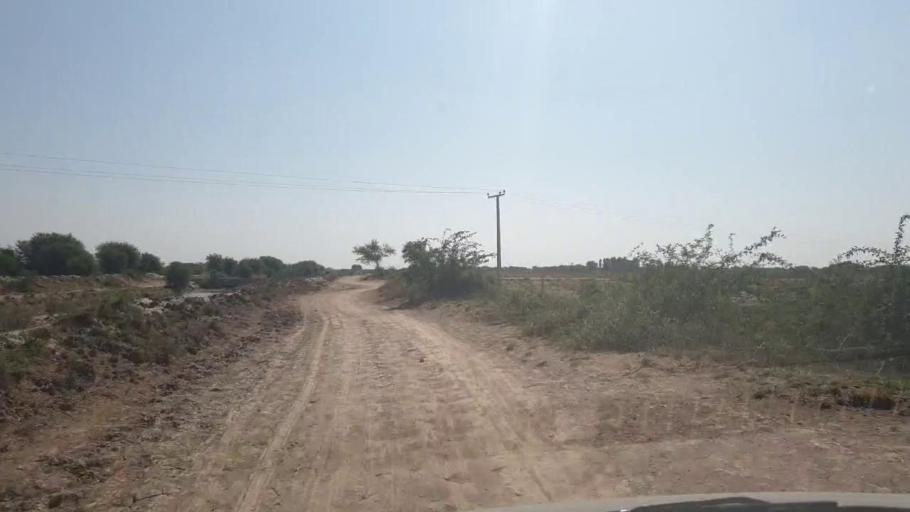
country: PK
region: Sindh
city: Digri
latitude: 24.9336
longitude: 69.1635
